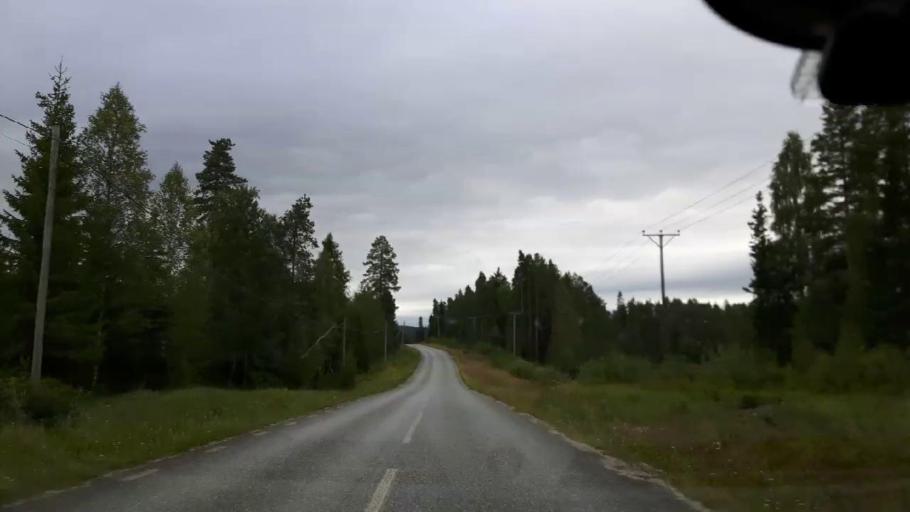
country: SE
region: Jaemtland
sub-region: Braecke Kommun
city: Braecke
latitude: 62.8803
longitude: 15.6179
